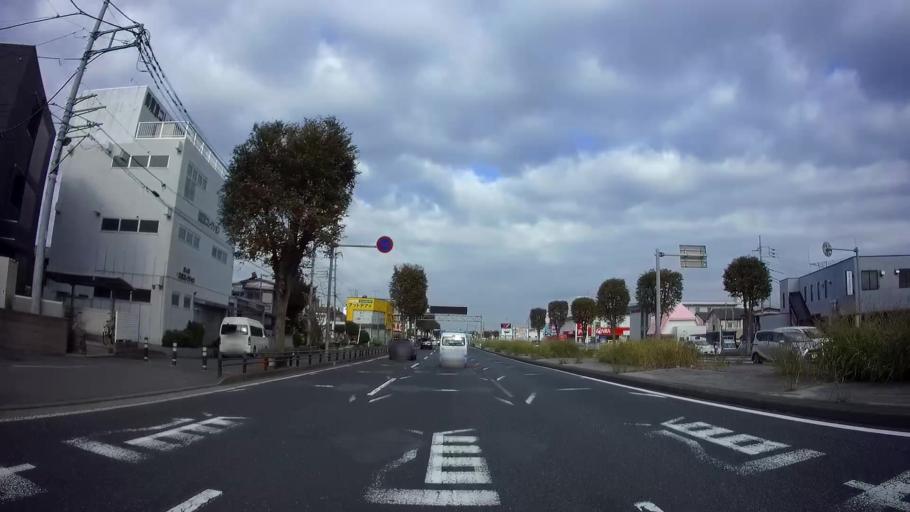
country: JP
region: Saitama
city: Yono
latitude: 35.8955
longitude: 139.6061
